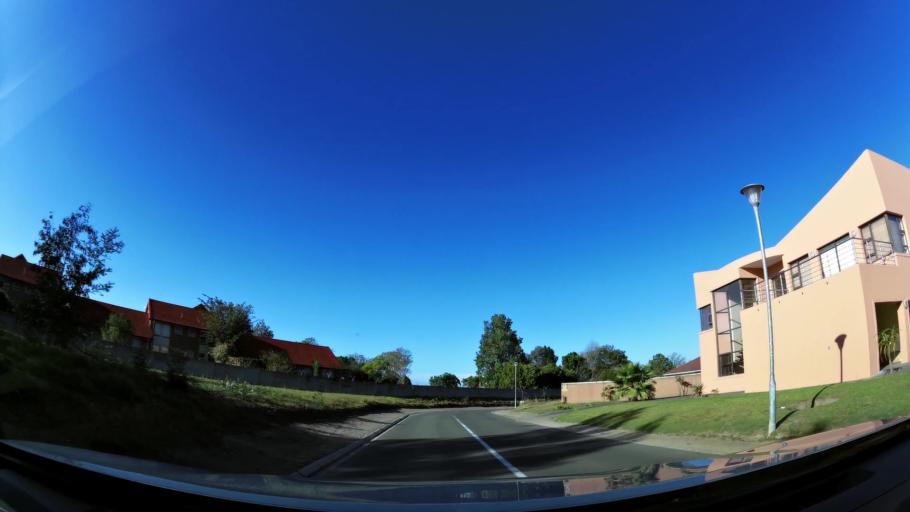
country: ZA
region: Western Cape
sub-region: Eden District Municipality
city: George
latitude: -33.9554
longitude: 22.4462
